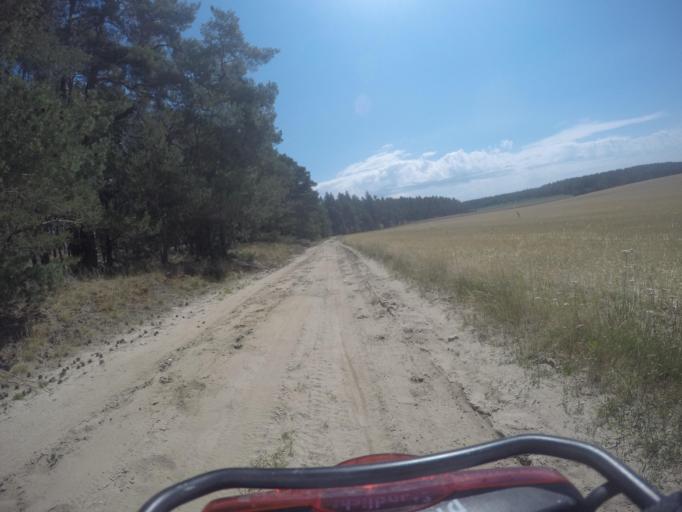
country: DE
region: Lower Saxony
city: Dahlem
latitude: 53.2269
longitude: 10.7233
